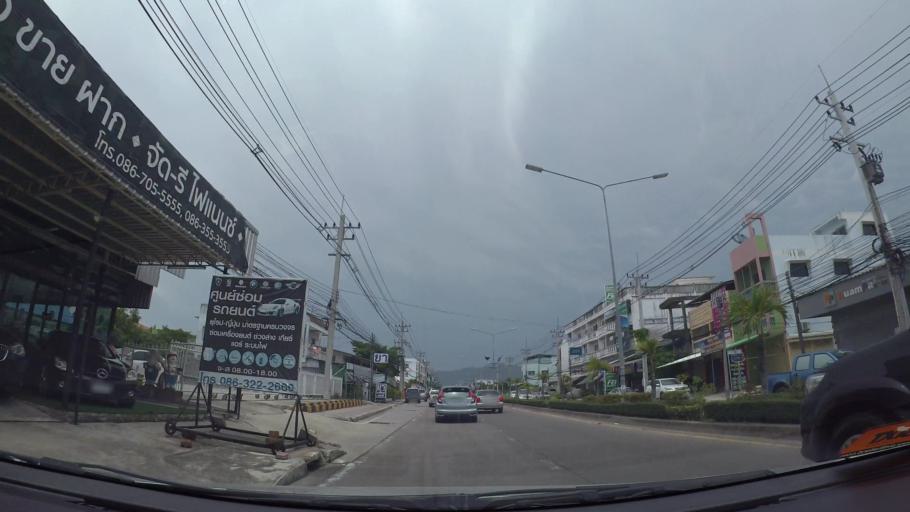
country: TH
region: Chon Buri
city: Chon Buri
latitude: 13.3462
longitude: 100.9842
